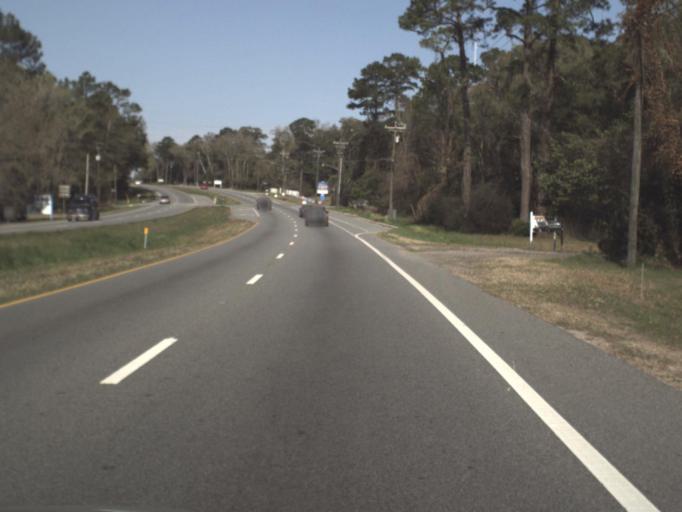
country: US
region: Florida
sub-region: Leon County
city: Tallahassee
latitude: 30.5063
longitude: -84.3324
